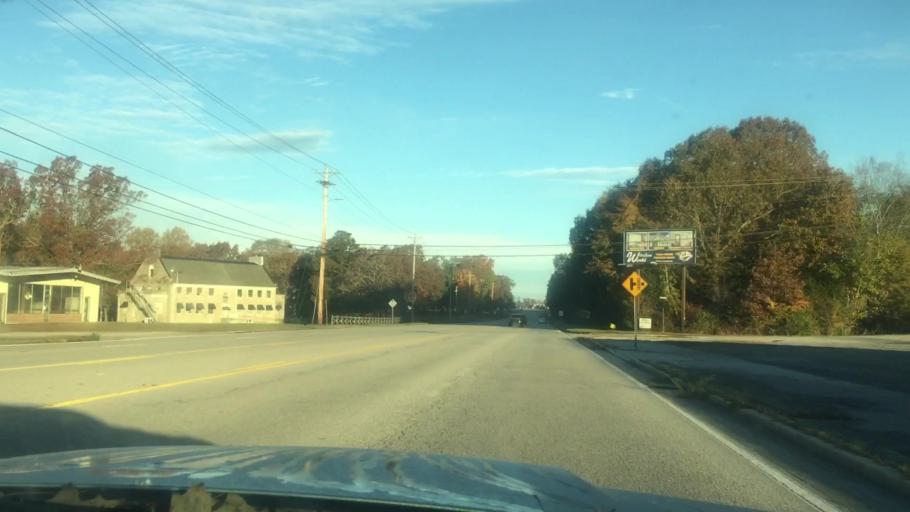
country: US
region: Tennessee
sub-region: Coffee County
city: Tullahoma
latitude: 35.3384
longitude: -86.1885
